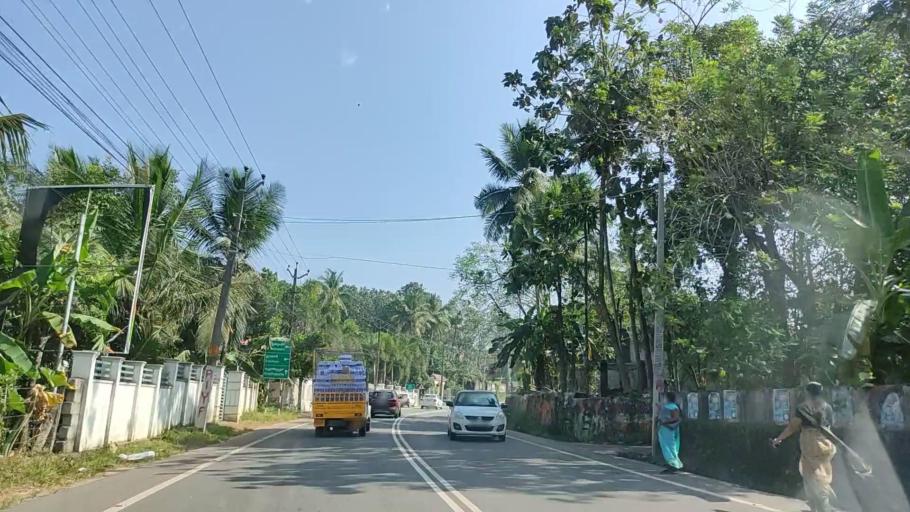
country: IN
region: Kerala
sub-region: Kollam
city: Punalur
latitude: 8.9353
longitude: 76.9442
